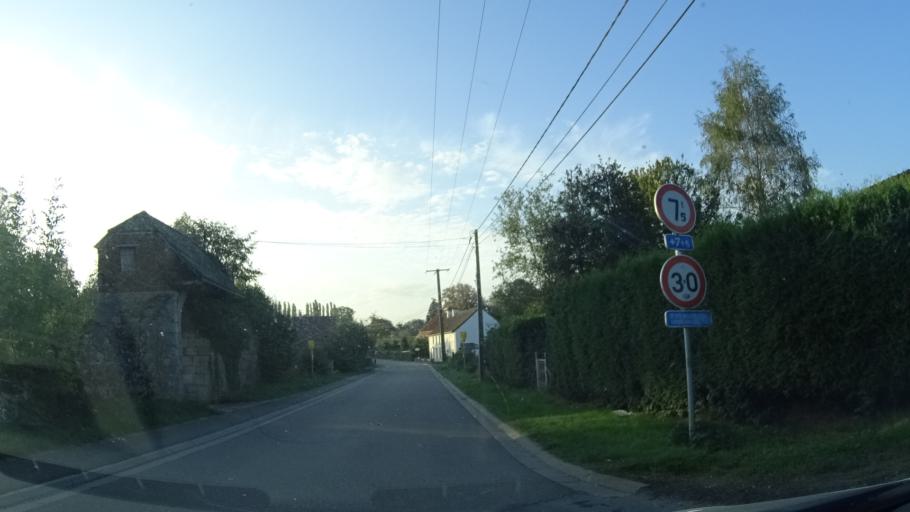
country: BE
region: Wallonia
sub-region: Province du Hainaut
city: Beaumont
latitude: 50.2623
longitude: 4.2316
